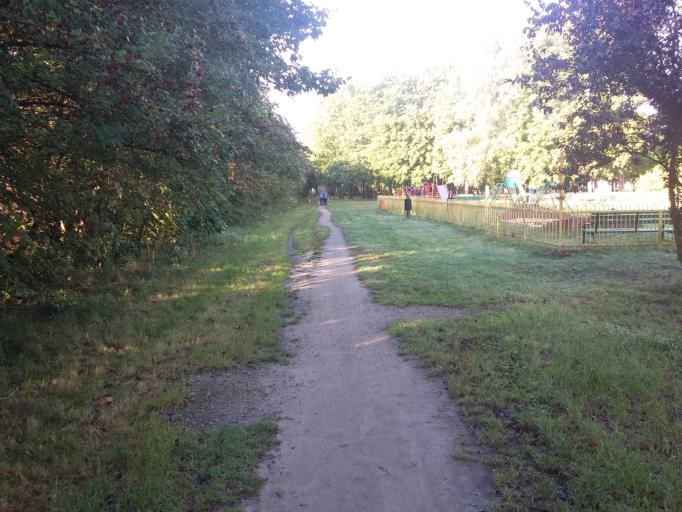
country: PL
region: Lodz Voivodeship
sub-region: Powiat pabianicki
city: Ksawerow
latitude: 51.7389
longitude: 19.4002
